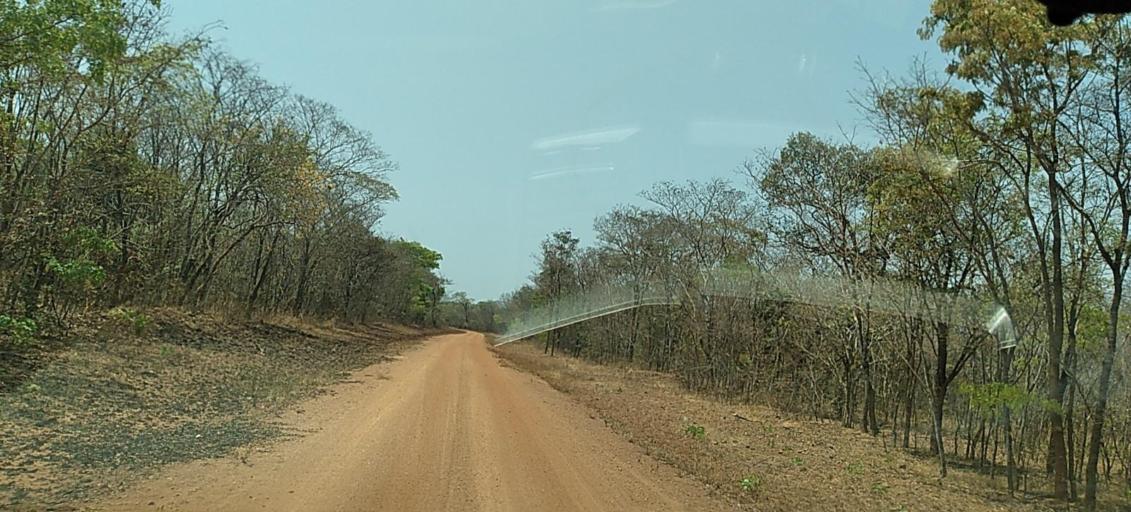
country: ZM
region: Central
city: Mumbwa
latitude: -14.2637
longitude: 26.5139
